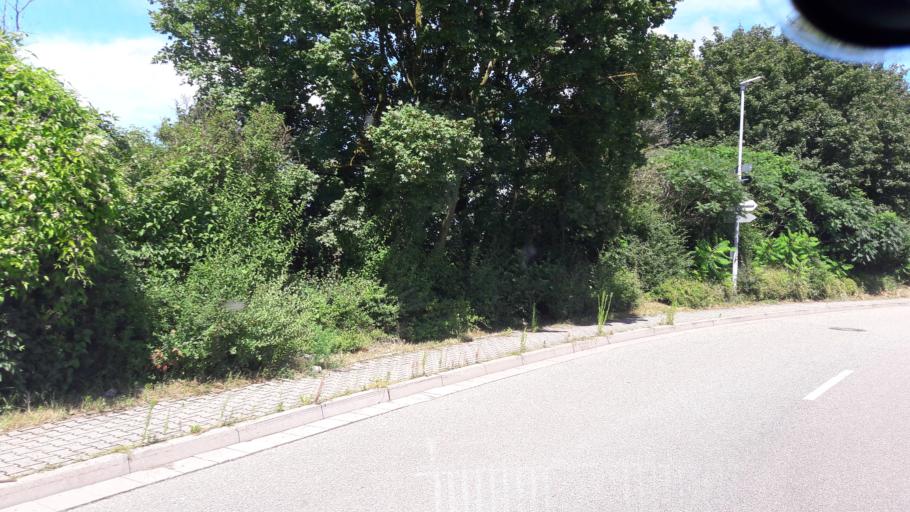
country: DE
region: Baden-Wuerttemberg
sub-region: Karlsruhe Region
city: Philippsburg
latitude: 49.2270
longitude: 8.4609
